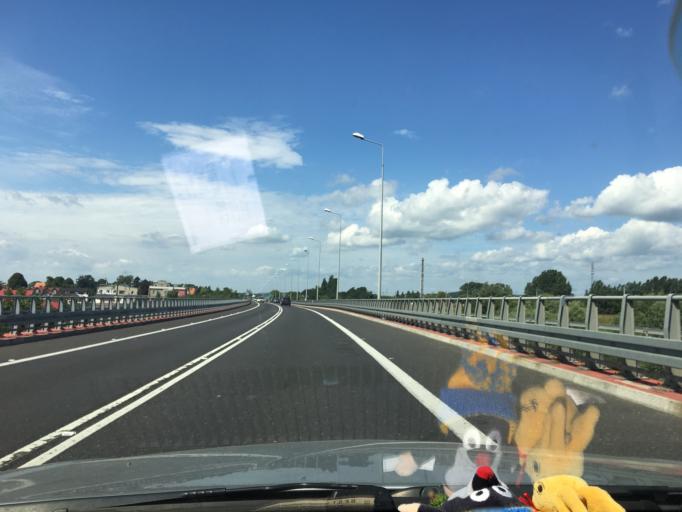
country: PL
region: West Pomeranian Voivodeship
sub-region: Powiat kamienski
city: Wolin
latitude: 53.8470
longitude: 14.6178
